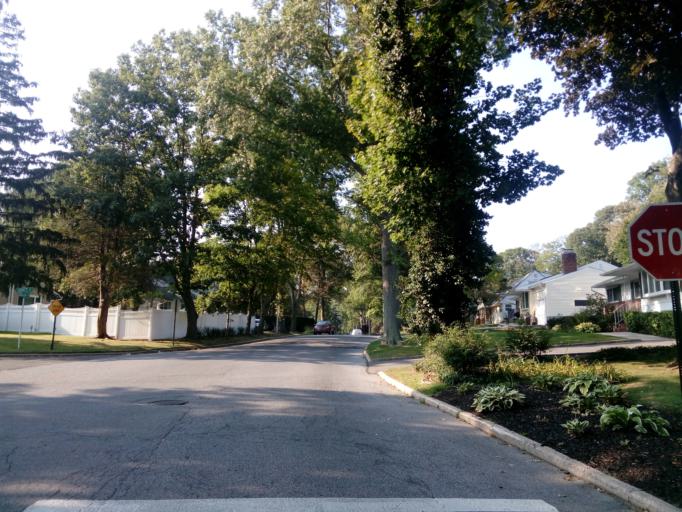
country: US
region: New York
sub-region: Nassau County
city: Locust Valley
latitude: 40.8581
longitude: -73.6020
